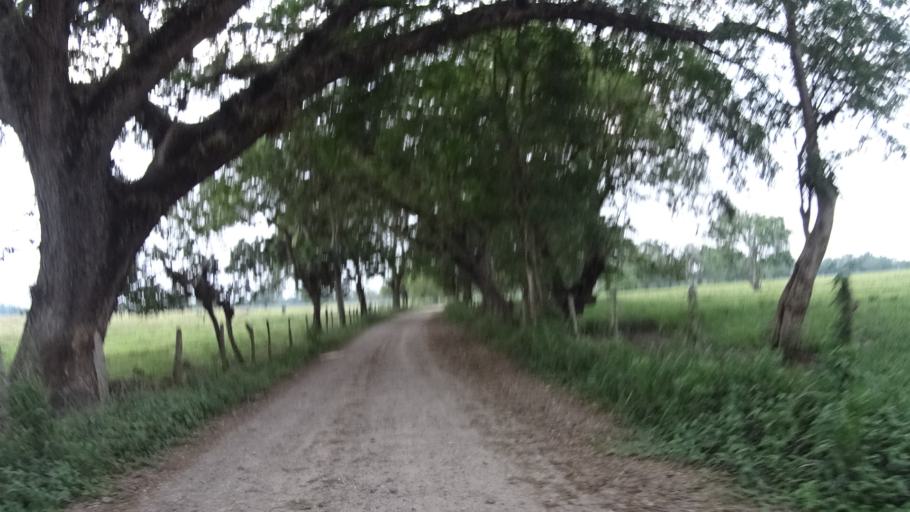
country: CO
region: Cundinamarca
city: Puerto Salgar
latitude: 5.4819
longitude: -74.6880
